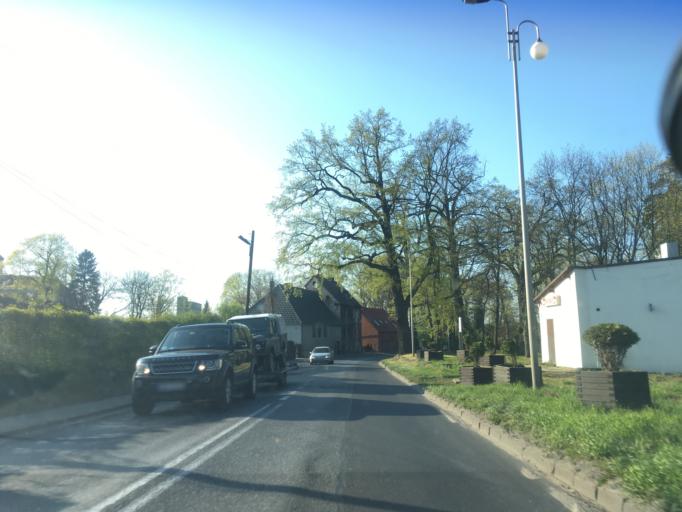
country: PL
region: Lubusz
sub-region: Powiat nowosolski
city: Kozuchow
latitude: 51.7464
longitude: 15.5976
